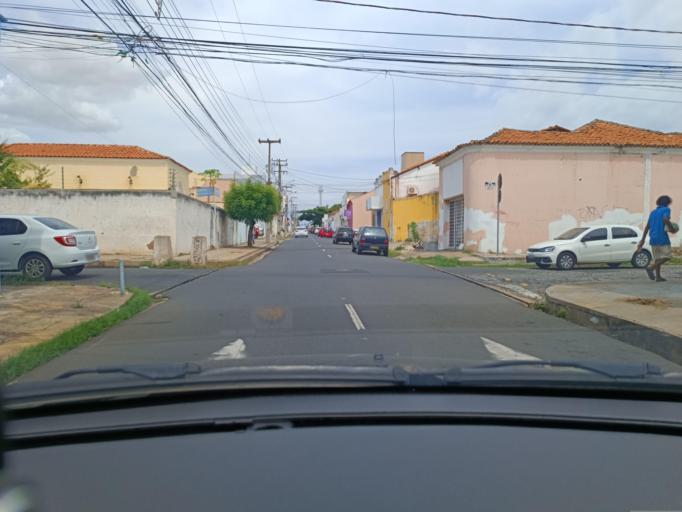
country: BR
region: Piaui
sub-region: Teresina
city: Teresina
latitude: -5.0921
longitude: -42.8084
